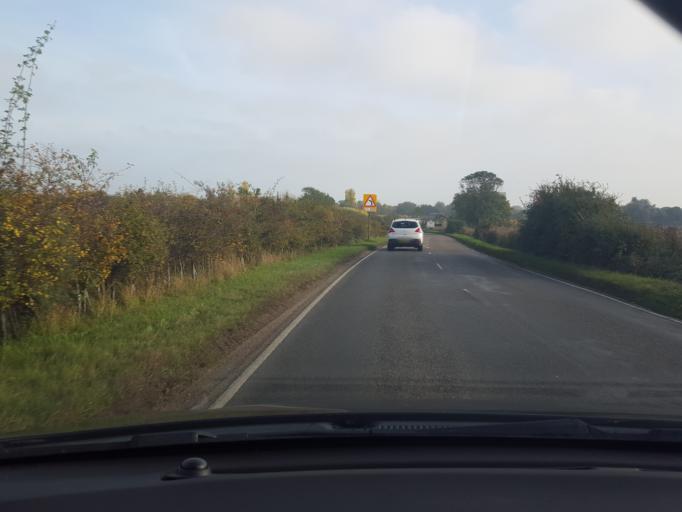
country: GB
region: England
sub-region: Essex
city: Frinton-on-Sea
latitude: 51.8555
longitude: 1.2122
